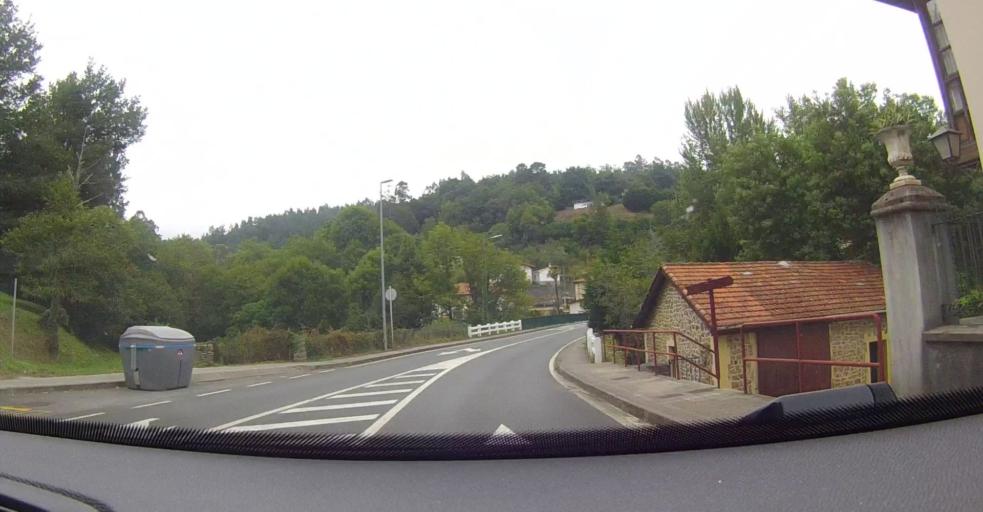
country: ES
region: Basque Country
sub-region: Bizkaia
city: Sopuerta
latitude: 43.2622
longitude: -3.1544
